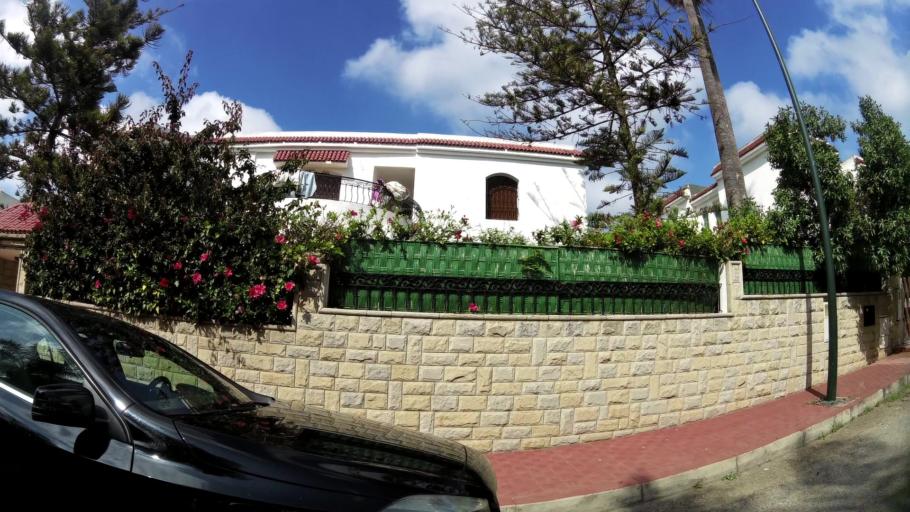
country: MA
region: Rabat-Sale-Zemmour-Zaer
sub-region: Skhirate-Temara
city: Temara
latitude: 33.9606
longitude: -6.8586
